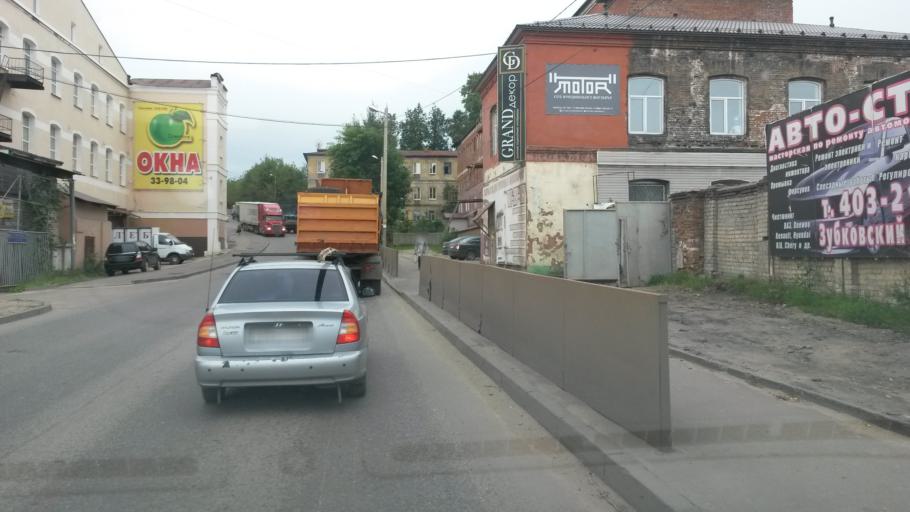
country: RU
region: Ivanovo
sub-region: Gorod Ivanovo
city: Ivanovo
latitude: 57.0124
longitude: 40.9533
